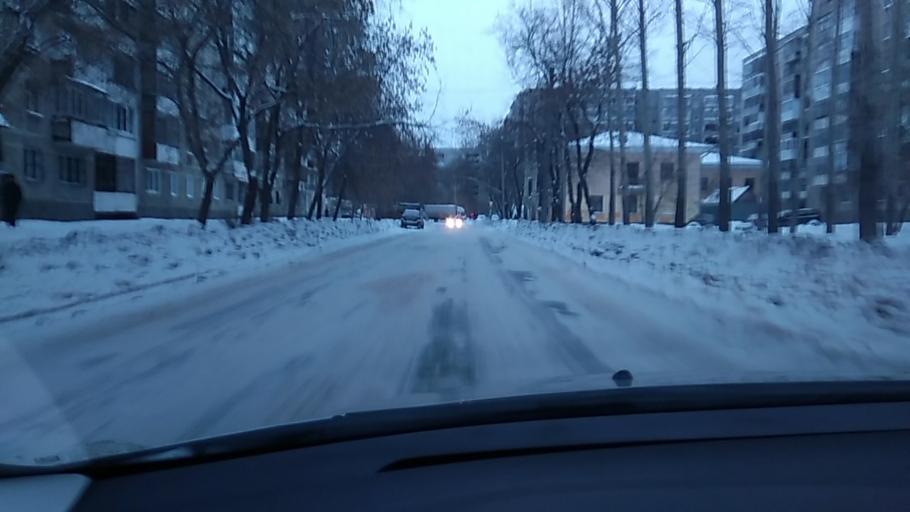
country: RU
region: Sverdlovsk
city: Yekaterinburg
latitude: 56.8946
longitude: 60.5983
